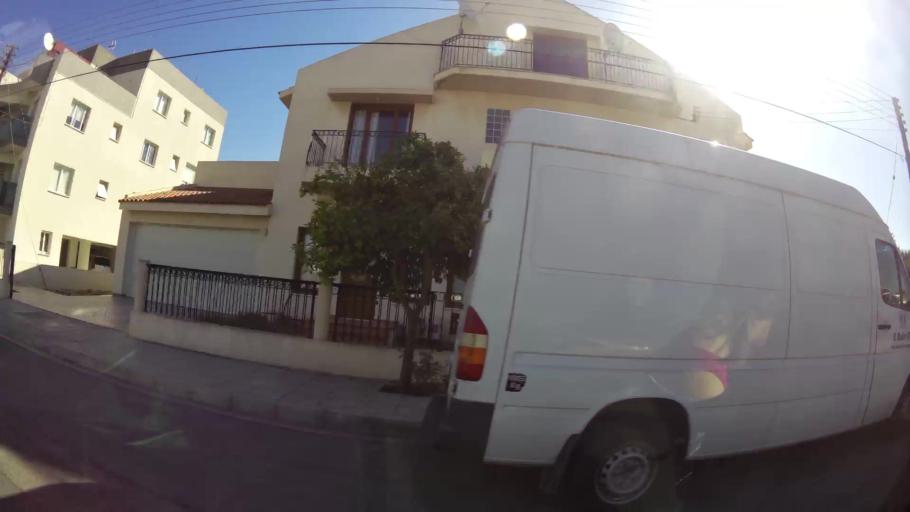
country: CY
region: Larnaka
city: Livadia
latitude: 34.9398
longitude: 33.6200
